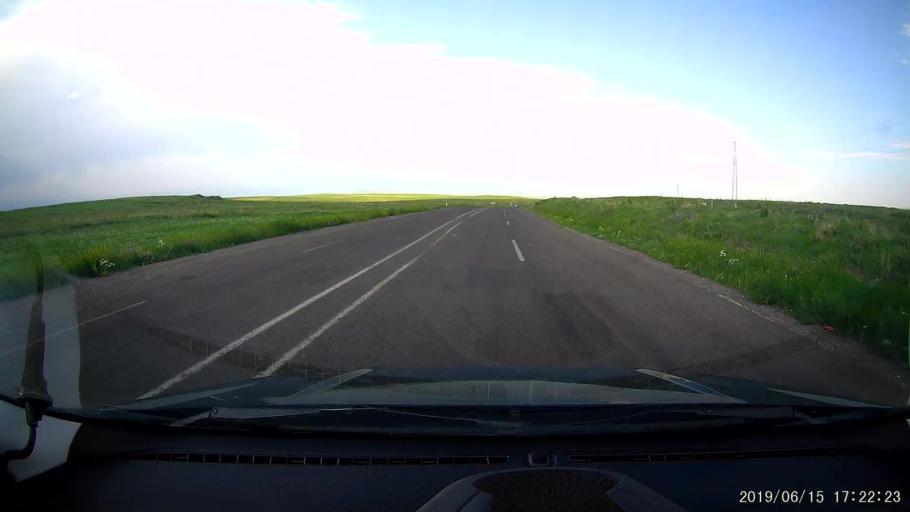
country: TR
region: Kars
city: Basgedikler
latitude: 40.6193
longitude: 43.3427
